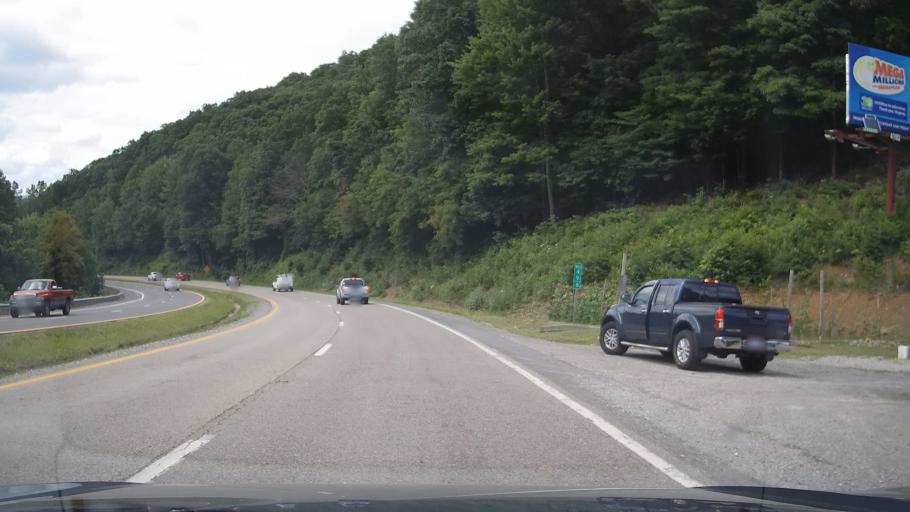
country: US
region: Virginia
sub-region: Wise County
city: Wise
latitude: 37.0200
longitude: -82.5884
